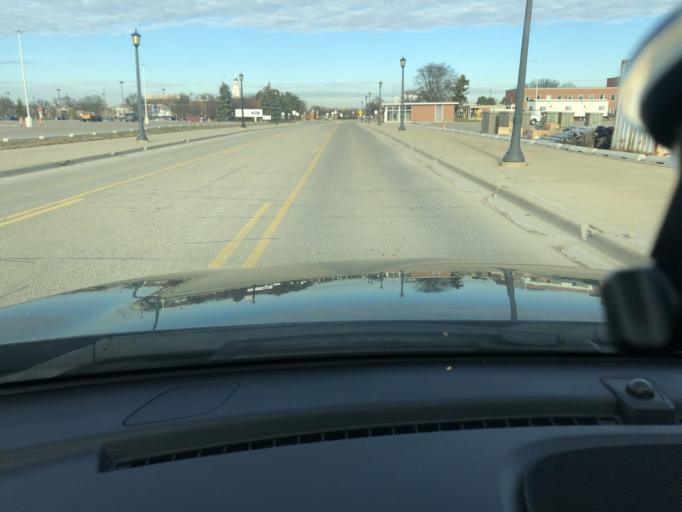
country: US
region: Michigan
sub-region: Wayne County
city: Allen Park
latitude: 42.2980
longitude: -83.2357
